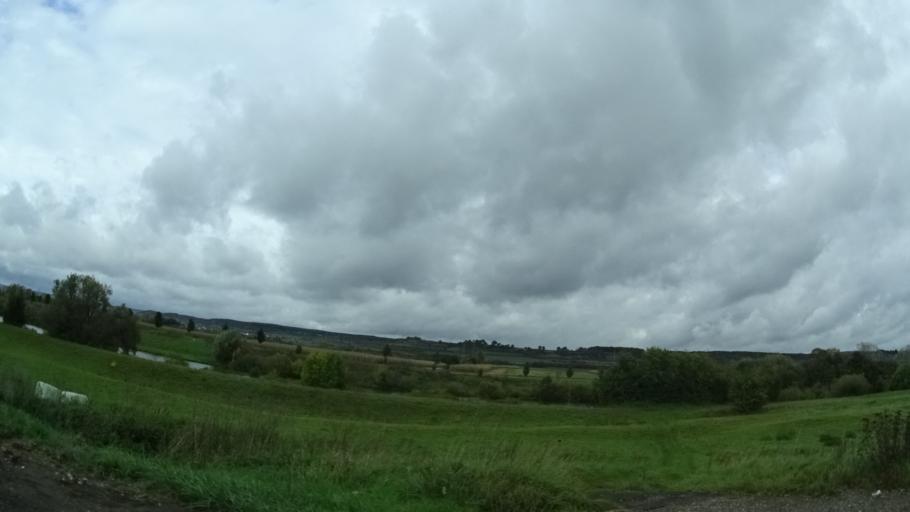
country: DE
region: Bavaria
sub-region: Upper Franconia
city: Viereth-Trunstadt
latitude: 49.9262
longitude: 10.7631
